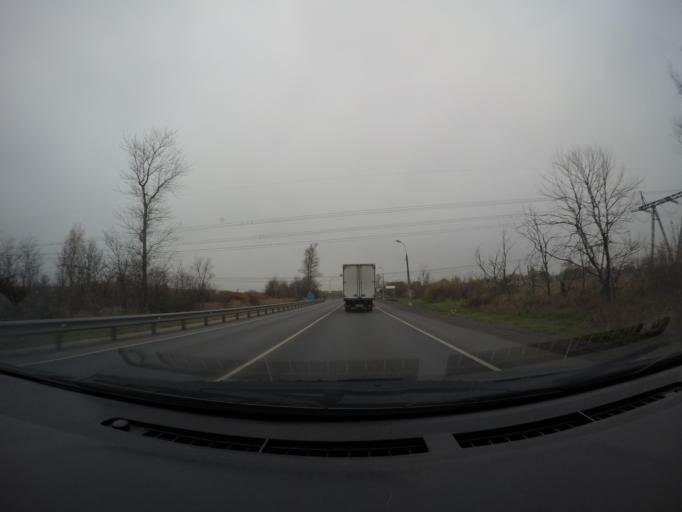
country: RU
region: Moskovskaya
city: Bronnitsy
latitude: 55.3879
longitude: 38.1956
